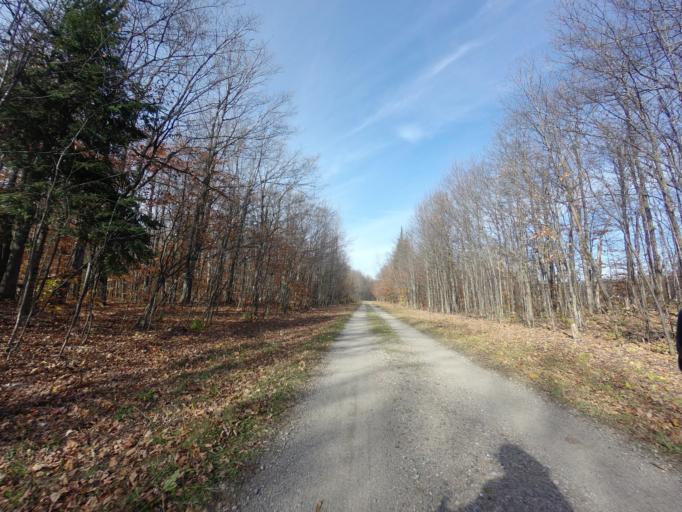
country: CA
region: Quebec
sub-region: Outaouais
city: Wakefield
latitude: 45.5150
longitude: -75.9092
